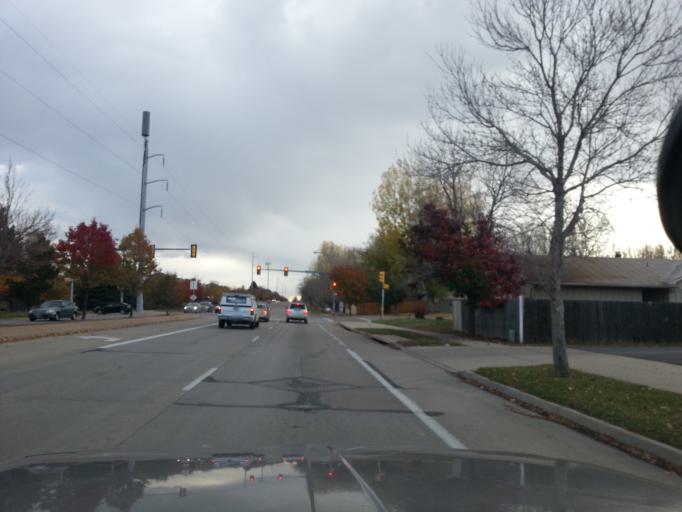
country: US
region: Colorado
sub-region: Larimer County
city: Fort Collins
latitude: 40.5527
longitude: -105.1059
